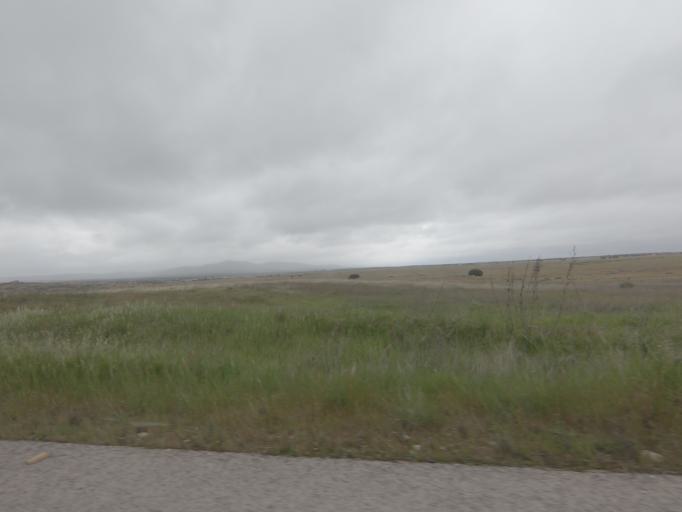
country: ES
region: Extremadura
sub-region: Provincia de Caceres
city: Malpartida de Caceres
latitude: 39.3483
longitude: -6.4710
